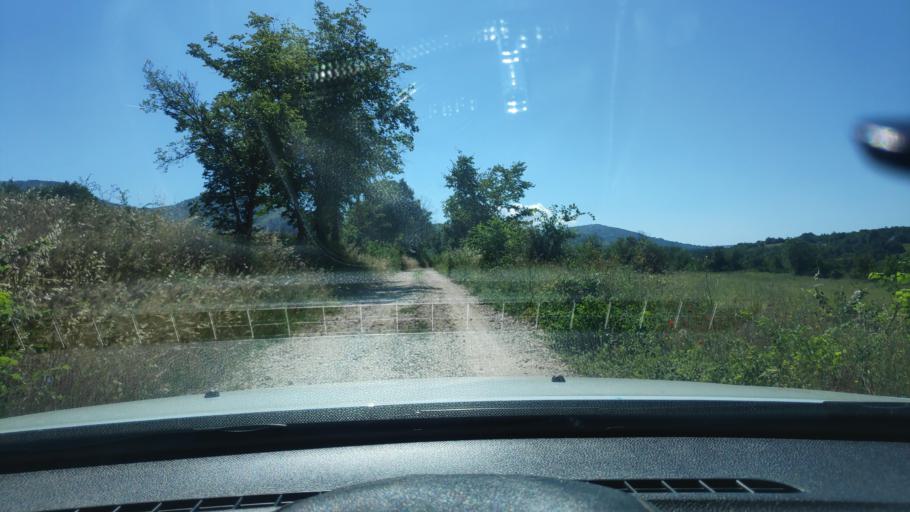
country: MK
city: Klechovce
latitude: 42.0713
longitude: 21.8824
